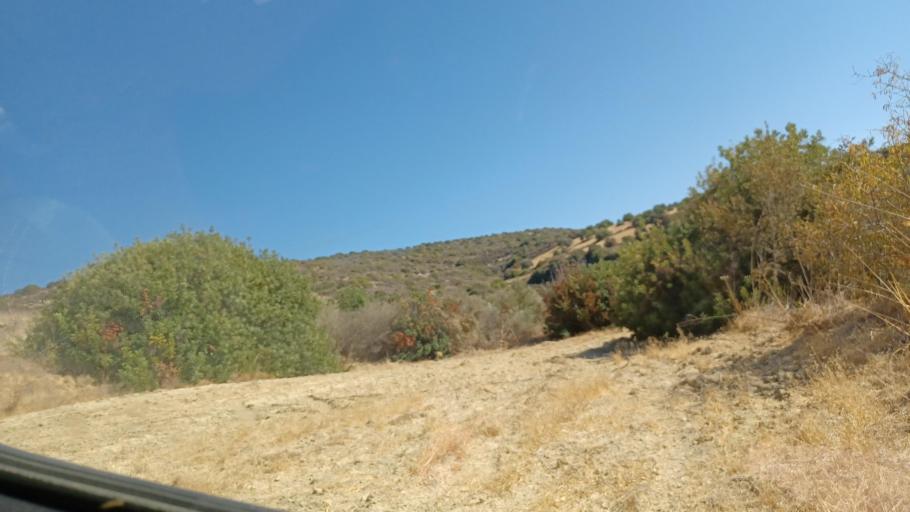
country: CY
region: Pafos
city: Polis
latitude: 34.9843
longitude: 32.4795
